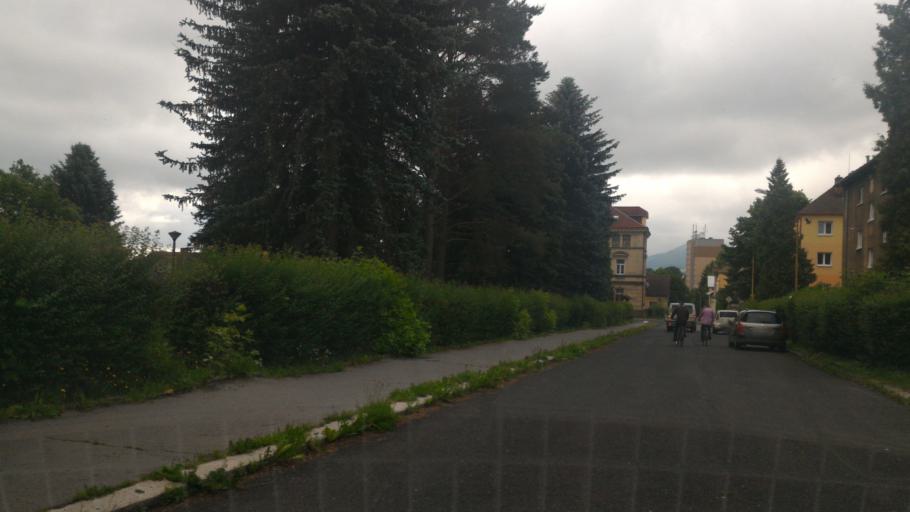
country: CZ
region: Ustecky
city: Varnsdorf
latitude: 50.9119
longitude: 14.6154
